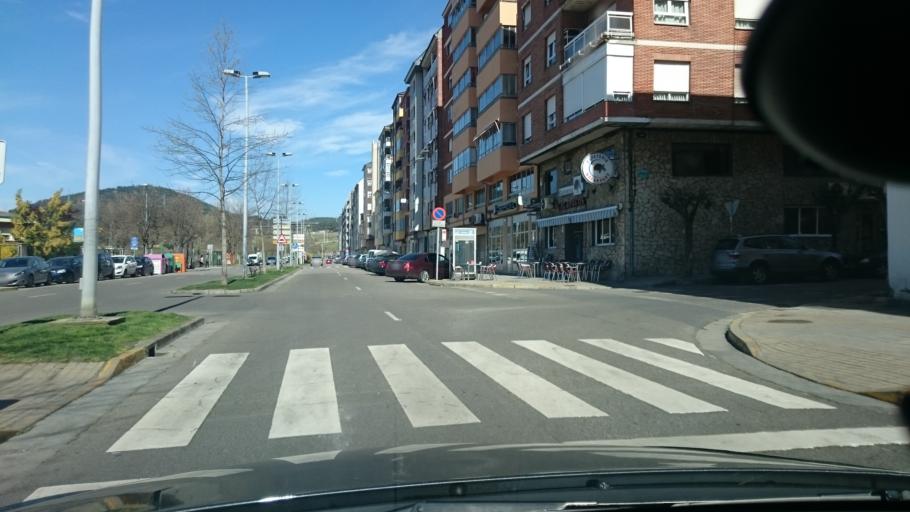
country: ES
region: Castille and Leon
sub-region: Provincia de Leon
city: Ponferrada
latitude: 42.5498
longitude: -6.5894
